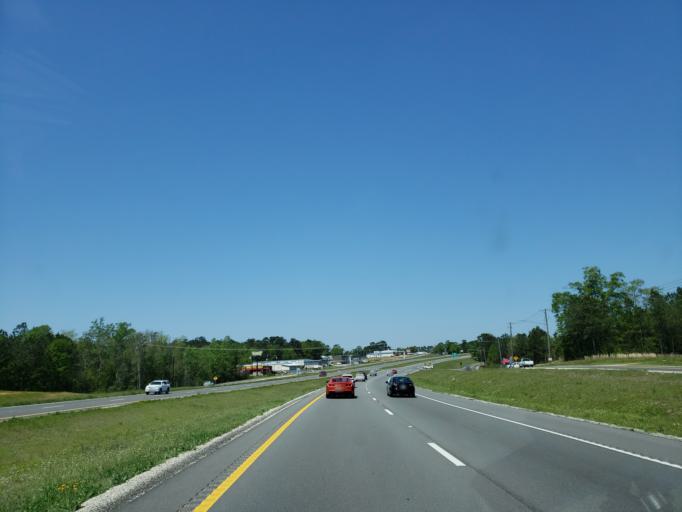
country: US
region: Mississippi
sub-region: Stone County
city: Wiggins
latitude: 30.8455
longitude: -89.1501
